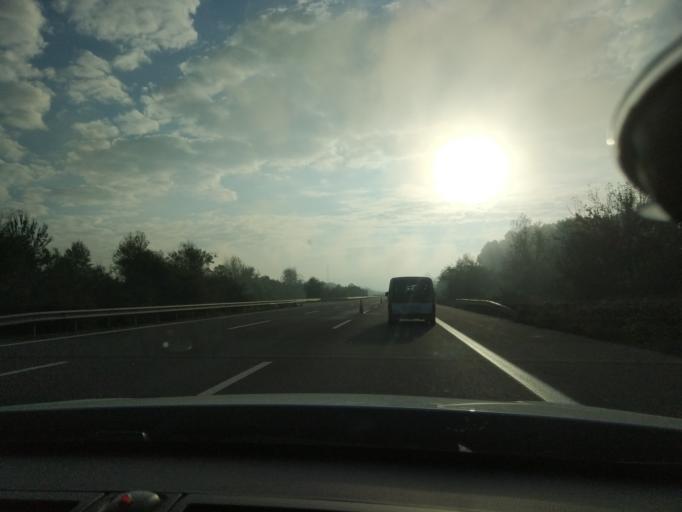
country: TR
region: Duzce
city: Duzce
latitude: 40.8130
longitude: 31.1040
